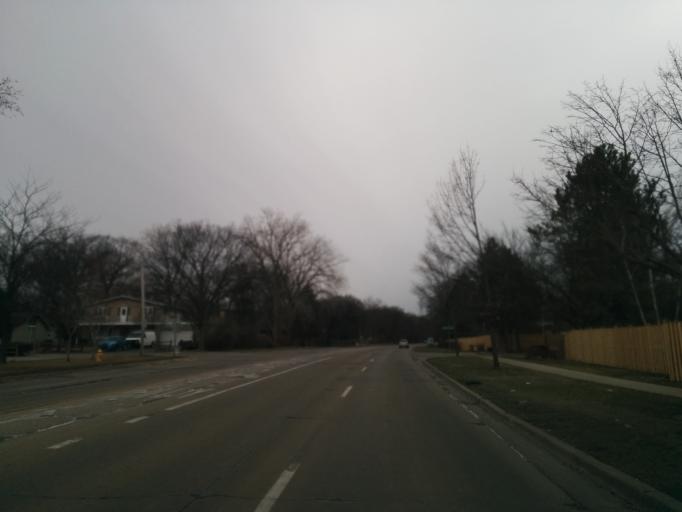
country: US
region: Illinois
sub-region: Cook County
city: Des Plaines
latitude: 42.0866
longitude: -87.8747
